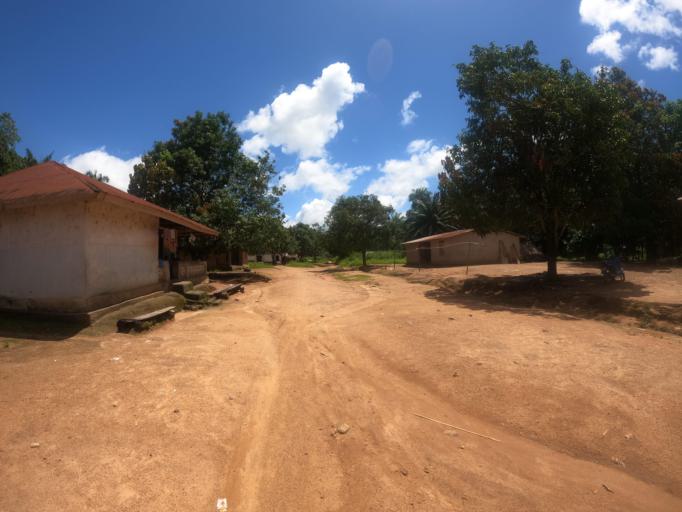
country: SL
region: Northern Province
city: Makeni
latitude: 8.8496
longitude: -12.1146
